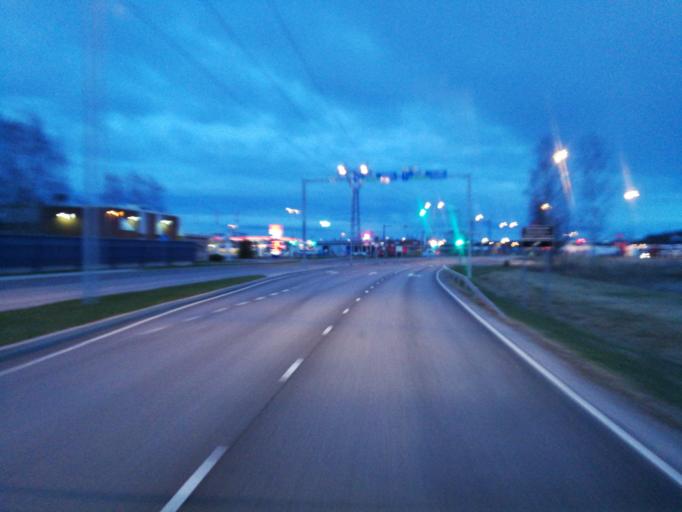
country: FI
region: Varsinais-Suomi
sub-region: Turku
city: Raisio
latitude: 60.4507
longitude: 22.2003
